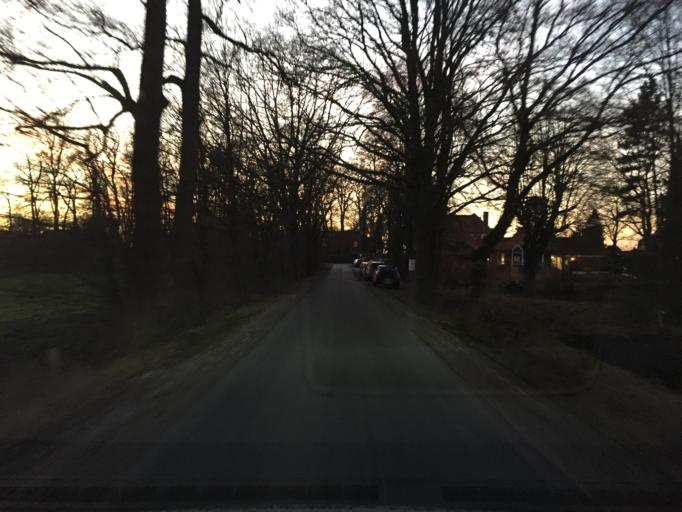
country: DE
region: Lower Saxony
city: Hassel
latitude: 52.6710
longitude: 8.8322
